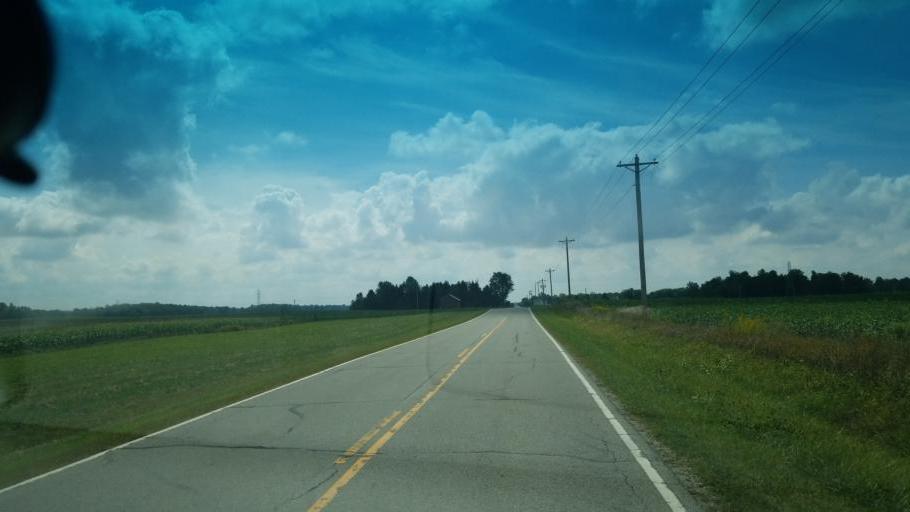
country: US
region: Ohio
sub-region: Crawford County
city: Bucyrus
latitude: 40.9540
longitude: -82.9017
